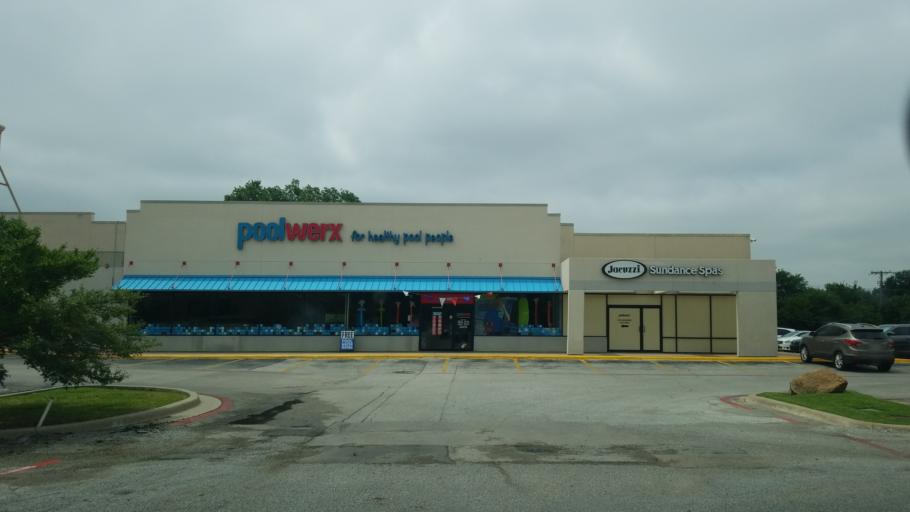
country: US
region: Texas
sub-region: Dallas County
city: Farmers Branch
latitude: 32.9090
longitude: -96.8600
